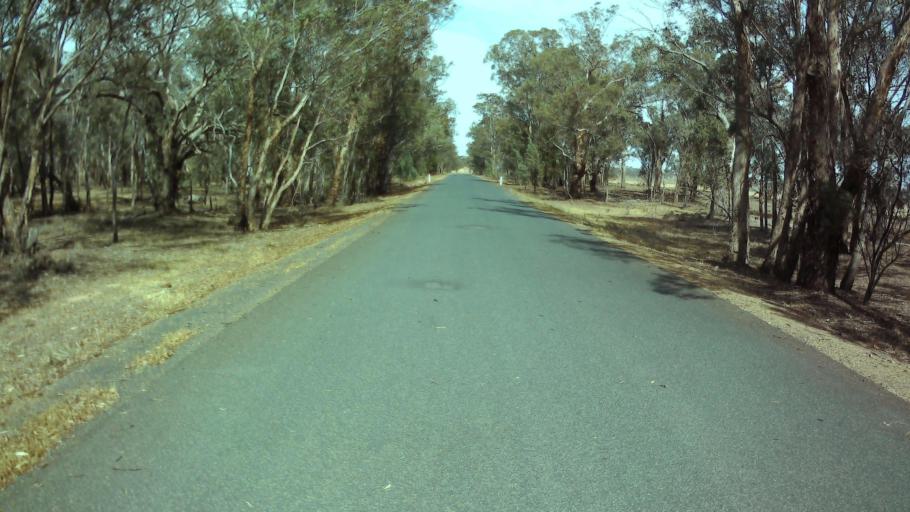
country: AU
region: New South Wales
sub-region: Weddin
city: Grenfell
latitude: -33.8085
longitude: 148.0755
